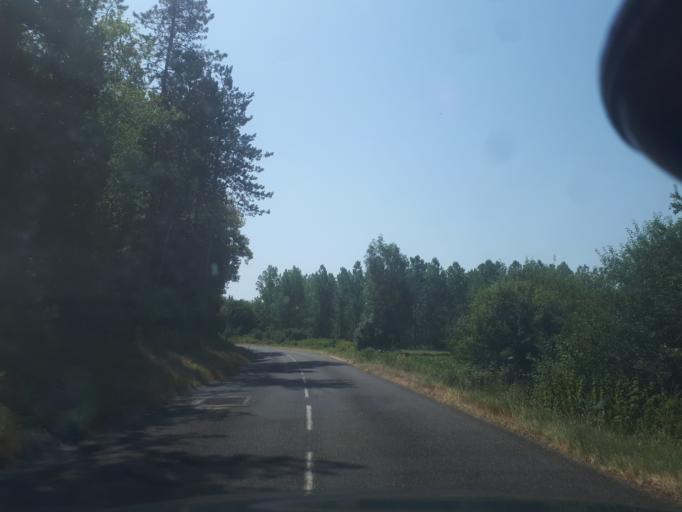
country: FR
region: Midi-Pyrenees
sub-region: Departement du Lot
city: Souillac
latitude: 44.8548
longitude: 1.4052
